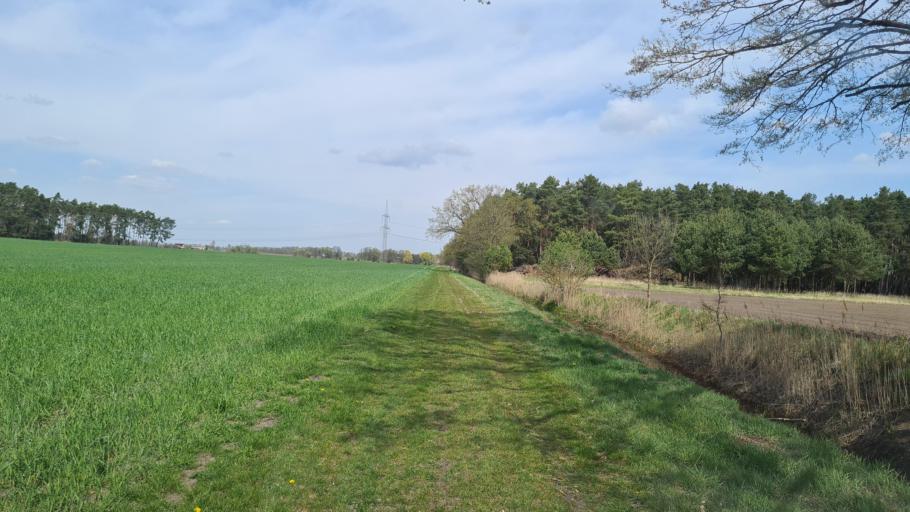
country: DE
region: Brandenburg
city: Finsterwalde
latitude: 51.6536
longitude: 13.6839
